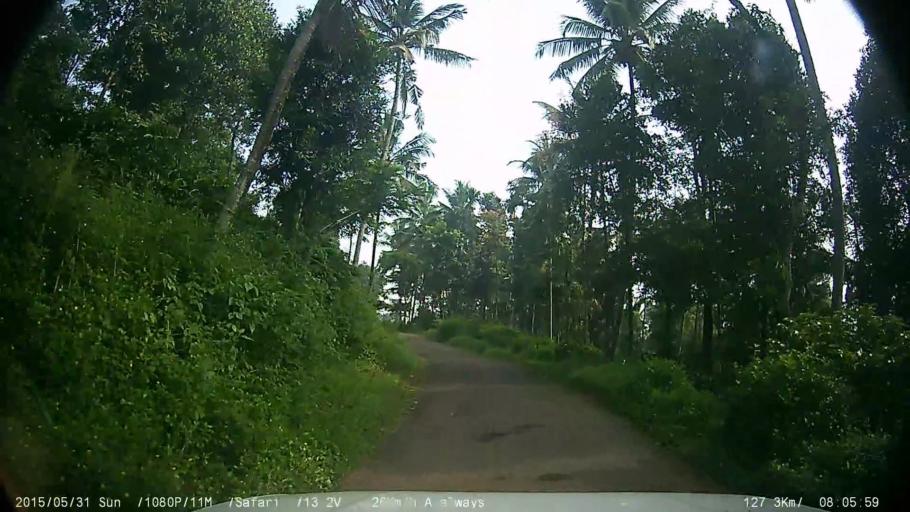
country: IN
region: Kerala
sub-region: Wayanad
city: Kalpetta
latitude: 11.6357
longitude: 76.0328
